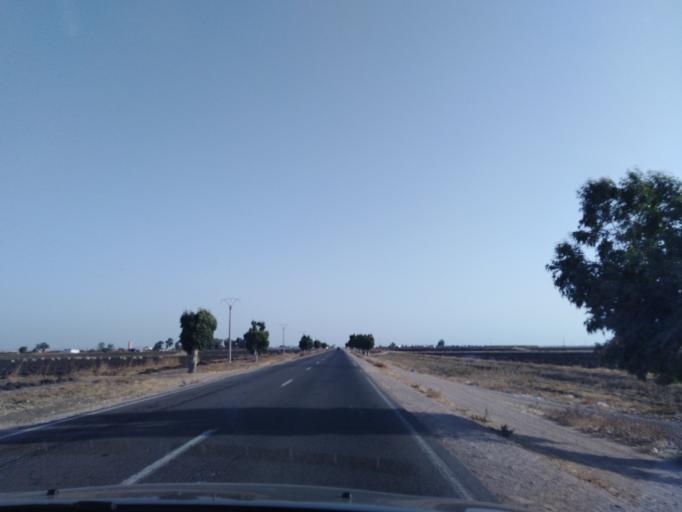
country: MA
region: Doukkala-Abda
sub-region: Safi
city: Youssoufia
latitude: 32.4771
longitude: -8.7706
